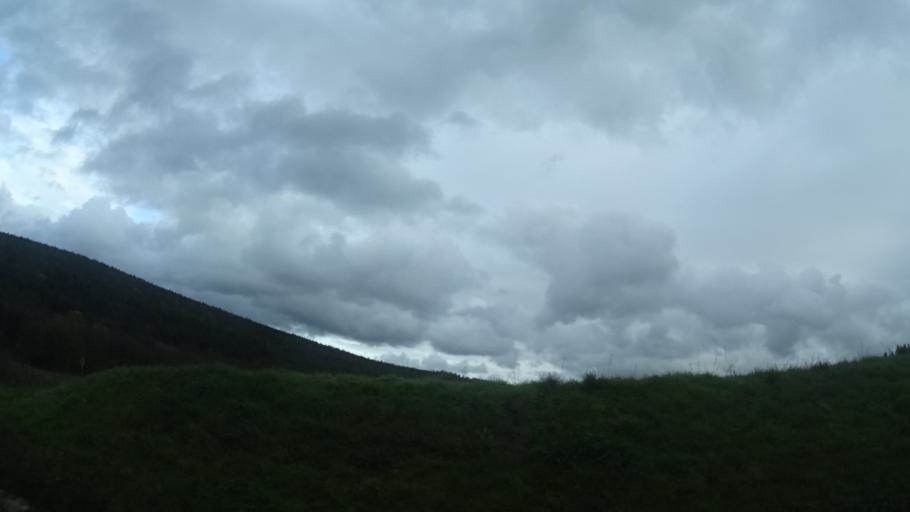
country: DE
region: Bavaria
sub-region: Regierungsbezirk Unterfranken
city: Hohenroth
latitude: 50.3539
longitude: 10.1350
